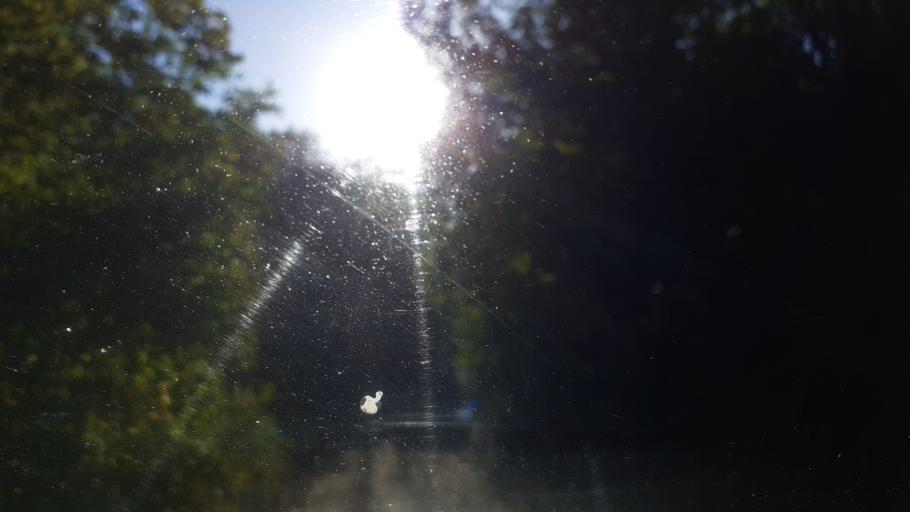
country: RU
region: Krasnodarskiy
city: Chernomorskiy
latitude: 44.6615
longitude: 38.4852
